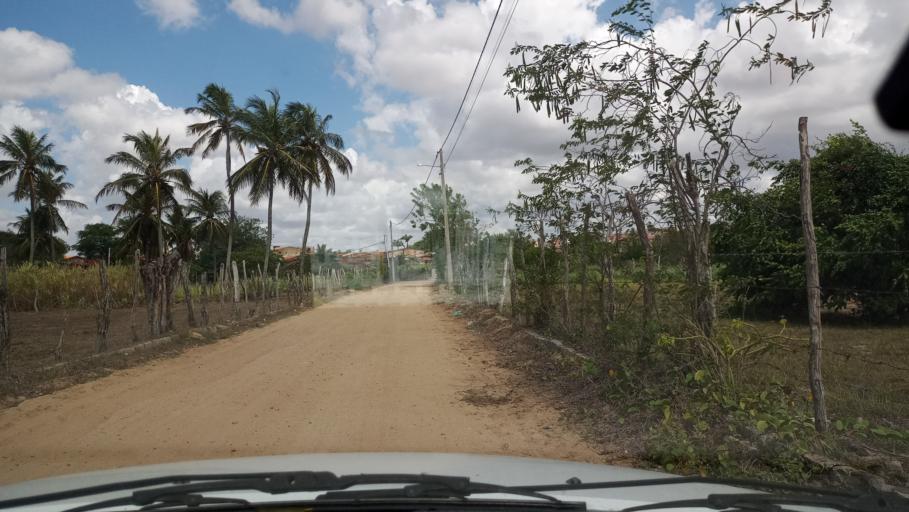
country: BR
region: Rio Grande do Norte
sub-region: Santo Antonio
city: Santo Antonio
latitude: -6.3503
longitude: -35.3726
